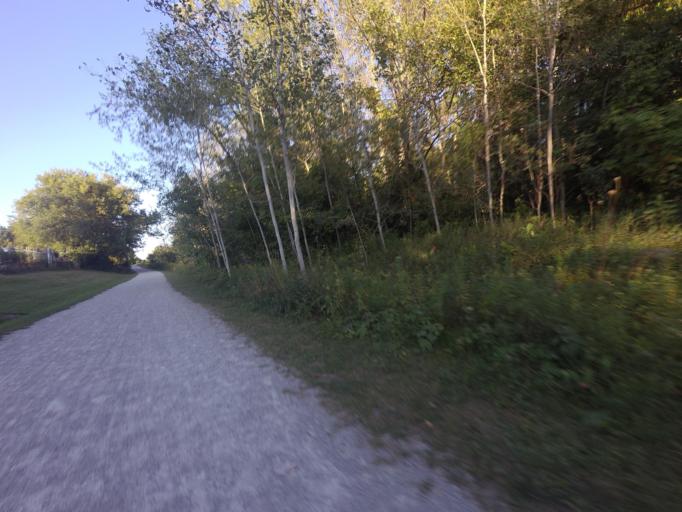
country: CA
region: Ontario
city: Brampton
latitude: 43.8703
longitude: -79.8629
